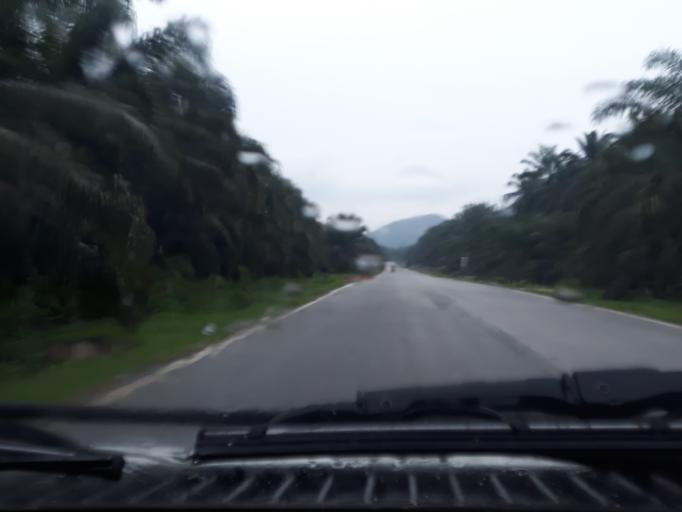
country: MY
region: Kedah
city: Kulim
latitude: 5.2546
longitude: 100.6039
